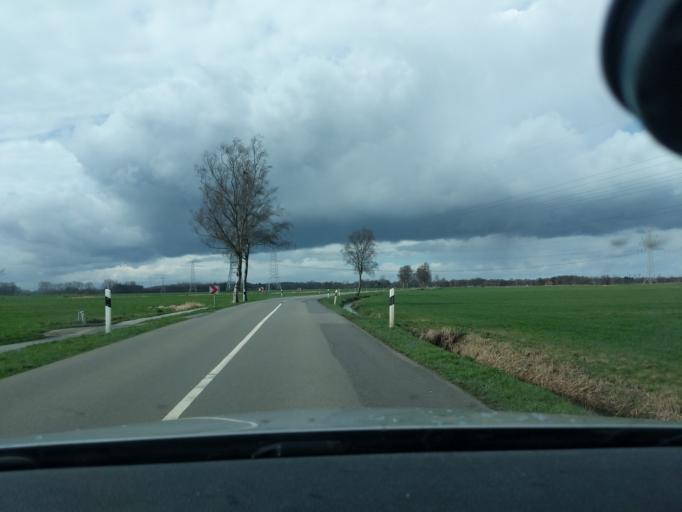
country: DE
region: Lower Saxony
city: Stade
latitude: 53.6195
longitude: 9.4496
